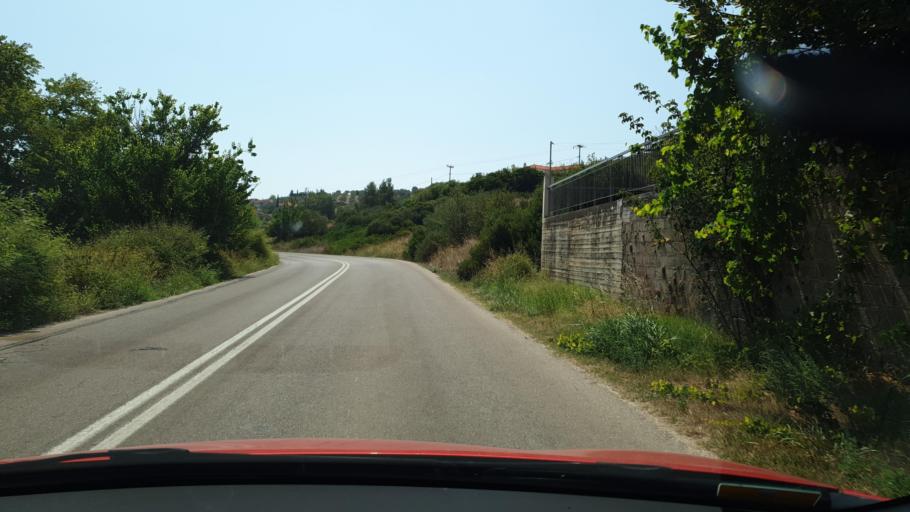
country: GR
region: Central Greece
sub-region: Nomos Evvoias
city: Aliveri
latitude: 38.4405
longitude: 24.1162
